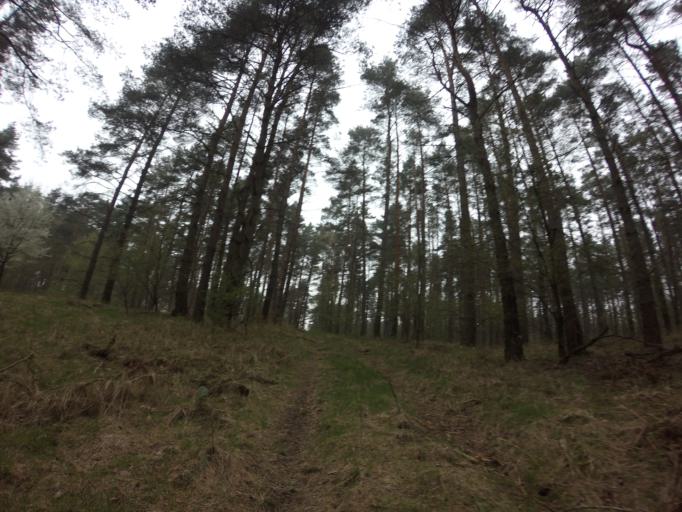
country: PL
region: West Pomeranian Voivodeship
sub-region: Powiat choszczenski
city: Recz
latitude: 53.1887
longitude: 15.5371
